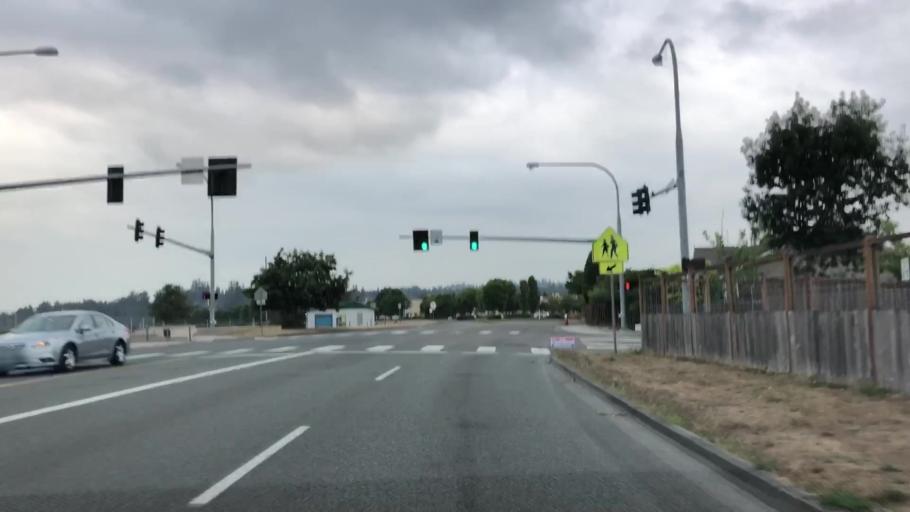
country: US
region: Washington
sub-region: Snohomish County
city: Monroe
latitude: 47.8622
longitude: -122.0095
